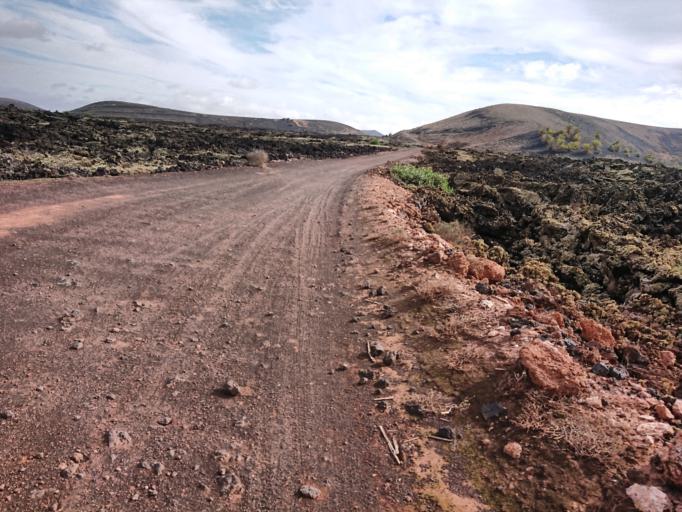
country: ES
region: Canary Islands
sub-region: Provincia de Las Palmas
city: Tinajo
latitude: 29.0224
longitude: -13.6801
